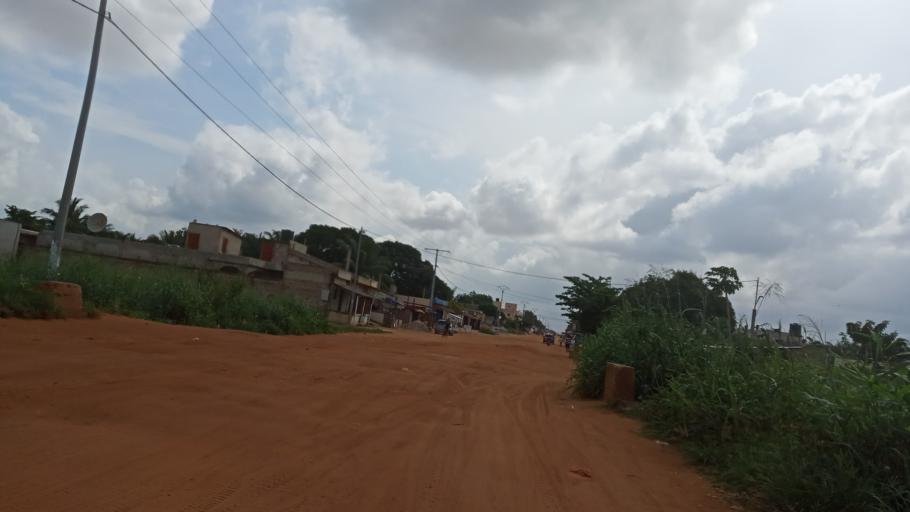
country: TG
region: Maritime
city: Lome
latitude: 6.2334
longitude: 1.1424
